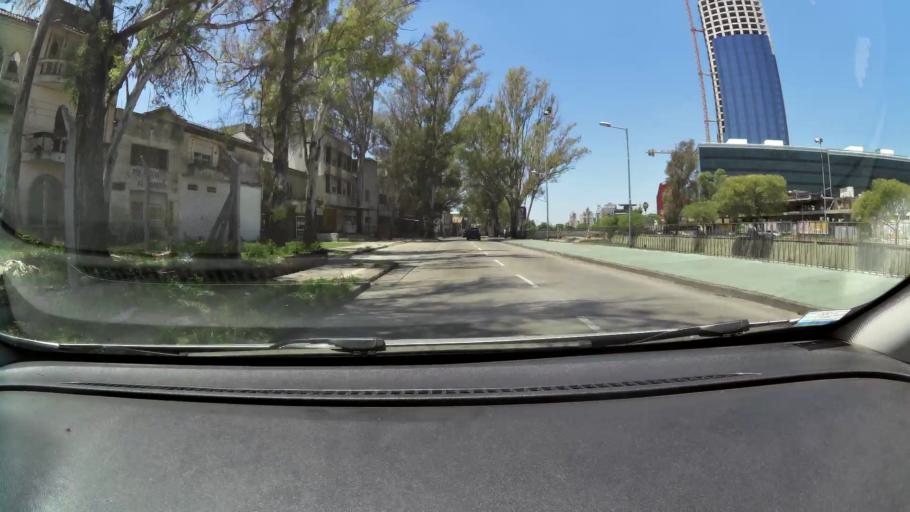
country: AR
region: Cordoba
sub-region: Departamento de Capital
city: Cordoba
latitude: -31.4058
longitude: -64.1921
